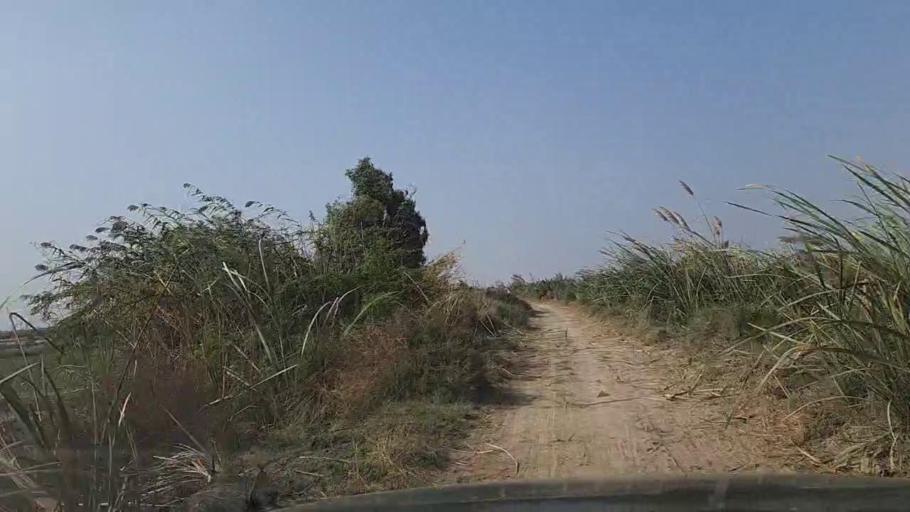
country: PK
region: Sindh
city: Gharo
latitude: 24.7220
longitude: 67.6689
